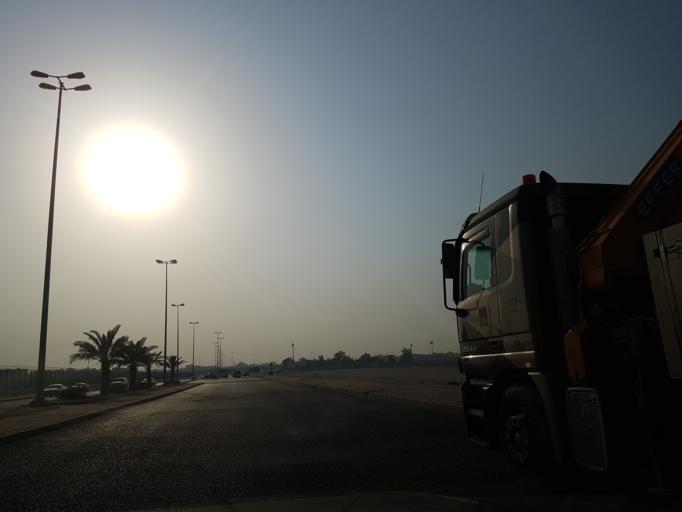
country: KW
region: Al Ahmadi
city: Al Manqaf
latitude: 29.1201
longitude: 48.1274
